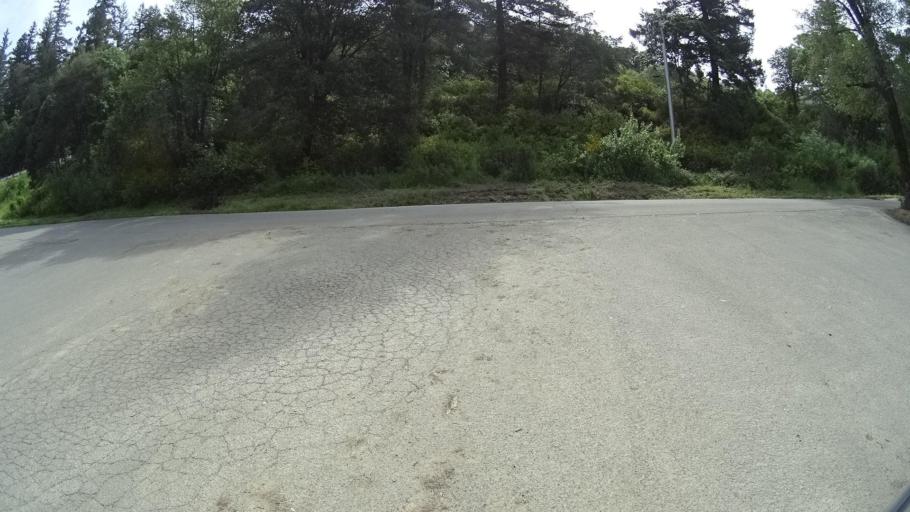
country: US
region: California
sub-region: Humboldt County
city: Redway
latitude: 40.1100
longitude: -123.7954
